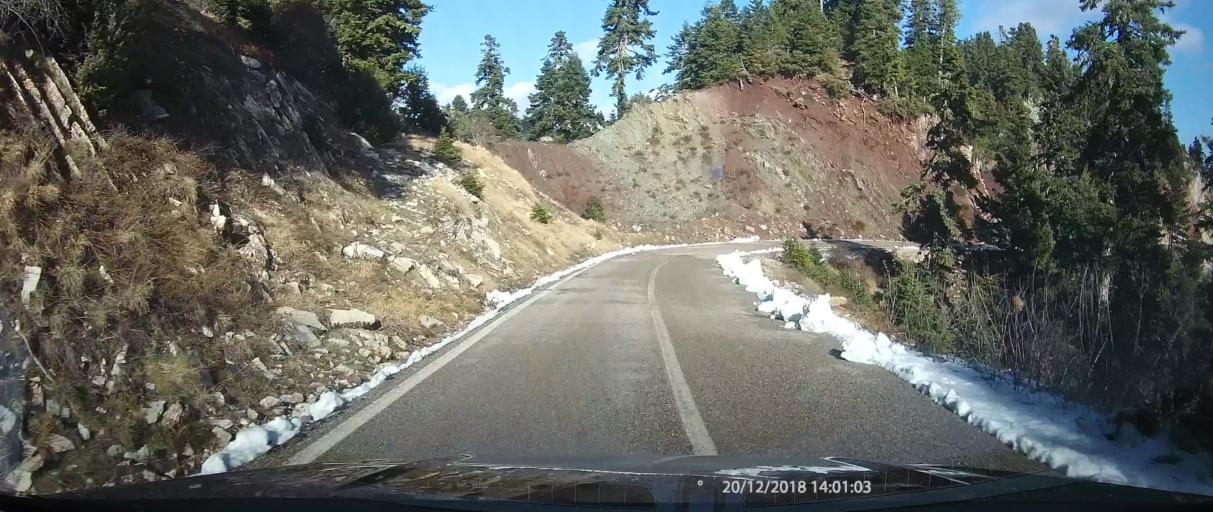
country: GR
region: West Greece
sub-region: Nomos Aitolias kai Akarnanias
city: Thermo
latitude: 38.7286
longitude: 21.6290
